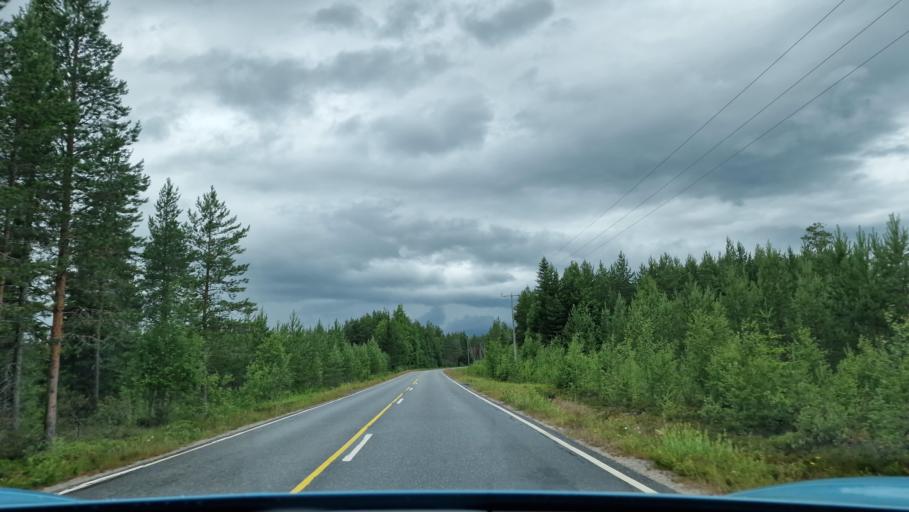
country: FI
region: Southern Ostrobothnia
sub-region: Jaerviseutu
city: Soini
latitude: 62.7385
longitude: 24.4181
